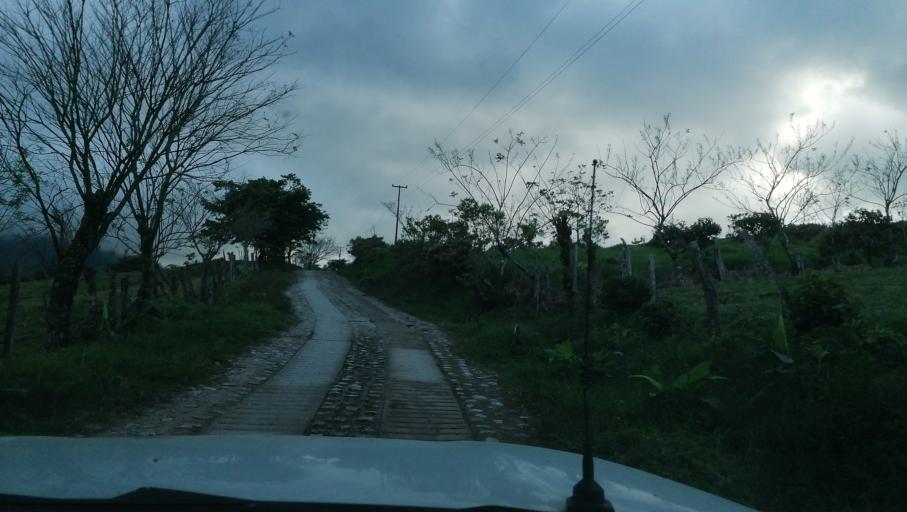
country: MX
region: Chiapas
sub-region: Francisco Leon
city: San Miguel la Sardina
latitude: 17.2963
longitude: -93.2653
